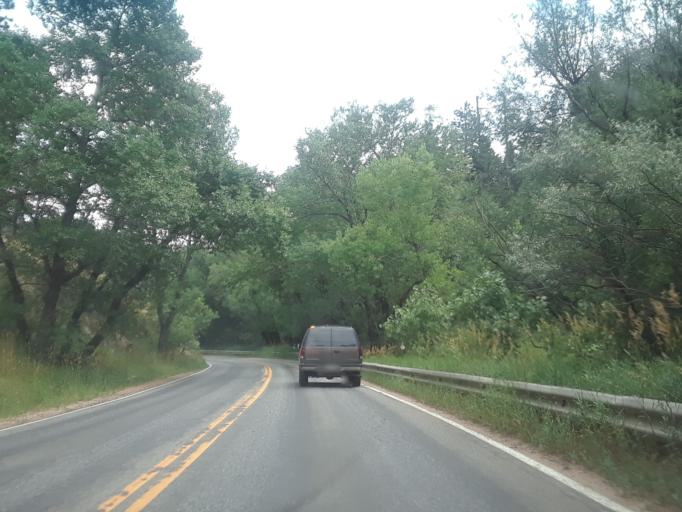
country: US
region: Colorado
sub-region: Boulder County
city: Boulder
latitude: 40.0258
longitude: -105.3119
